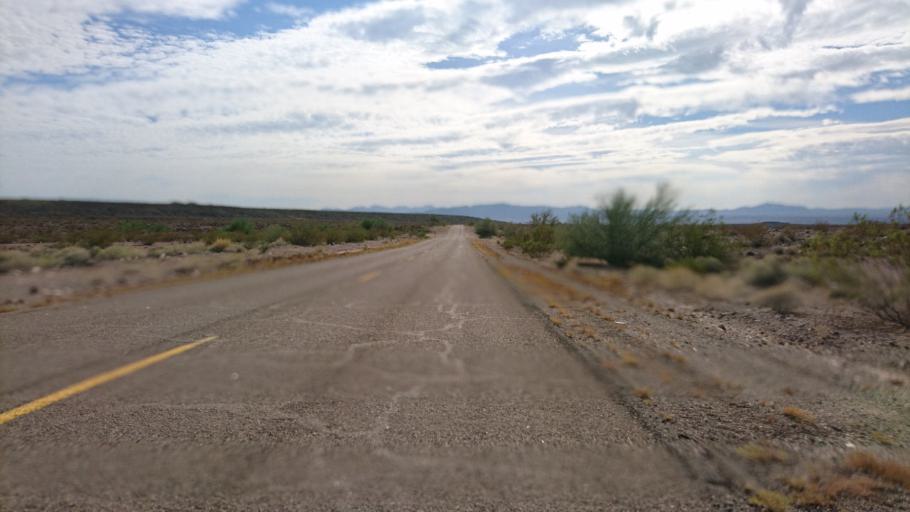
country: US
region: Arizona
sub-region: Mohave County
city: Mohave Valley
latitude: 34.8632
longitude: -114.4432
